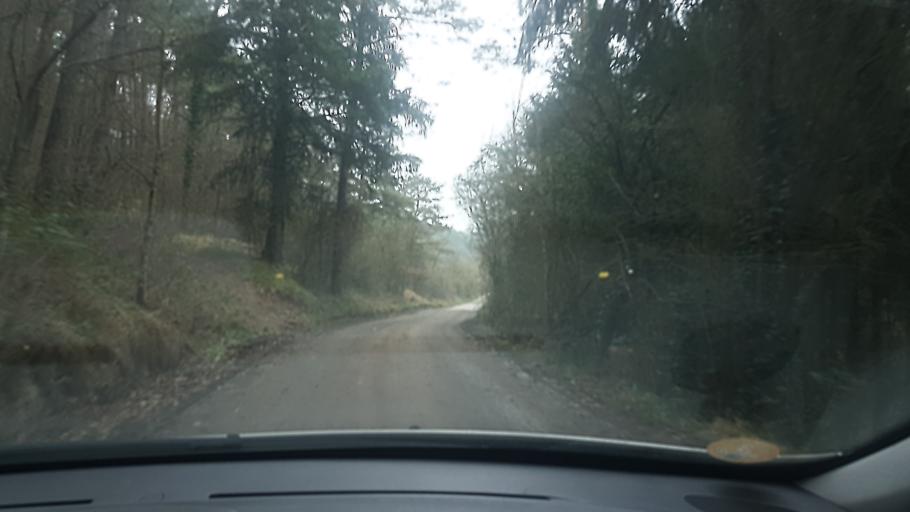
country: BE
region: Wallonia
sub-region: Province de Namur
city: Couvin
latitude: 50.0762
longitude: 4.5939
